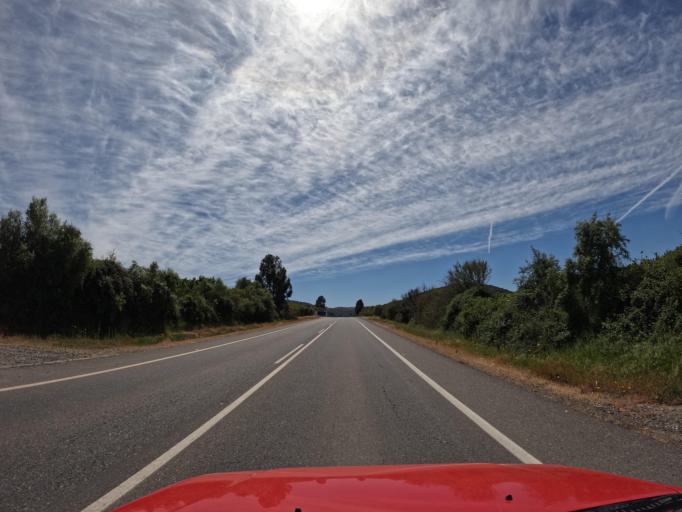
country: CL
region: Maule
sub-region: Provincia de Talca
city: Talca
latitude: -35.2688
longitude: -71.5404
